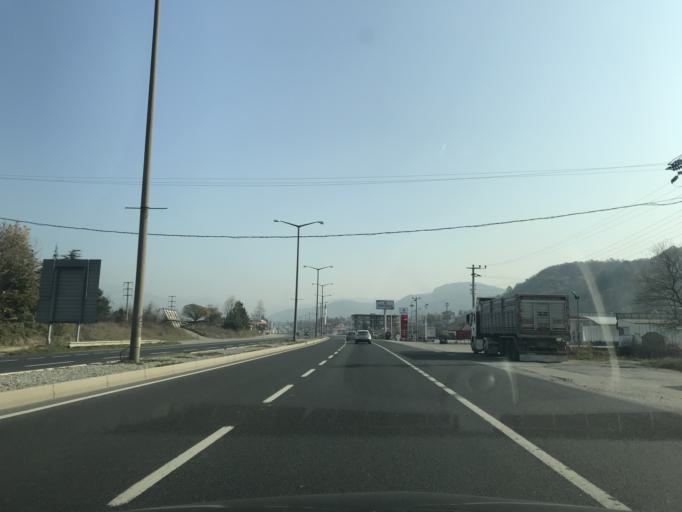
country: TR
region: Duzce
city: Kaynasli
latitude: 40.7798
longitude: 31.2835
